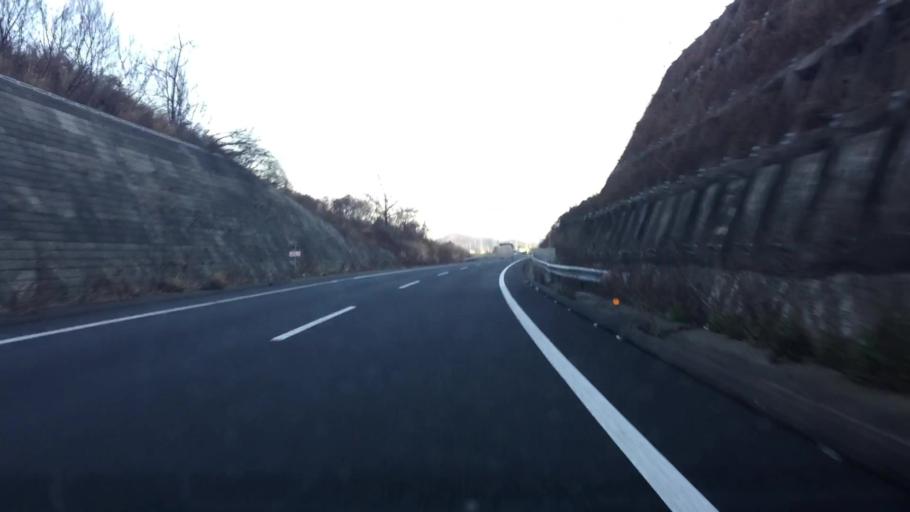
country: JP
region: Tochigi
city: Tanuma
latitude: 36.3718
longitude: 139.5404
